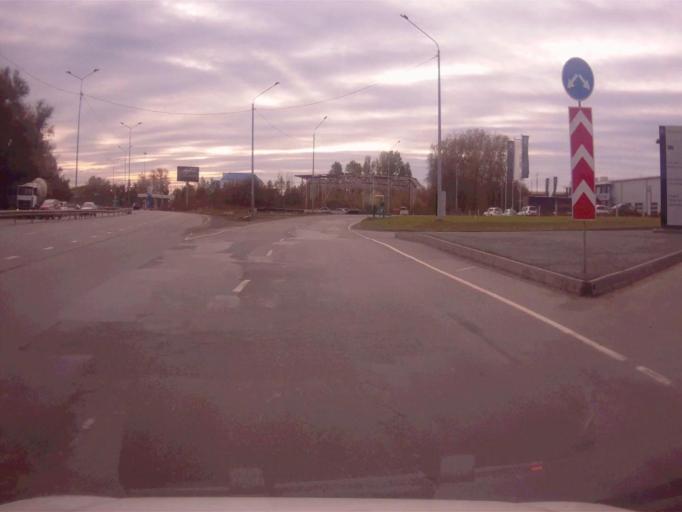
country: RU
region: Chelyabinsk
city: Novosineglazovskiy
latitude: 55.0822
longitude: 61.3926
